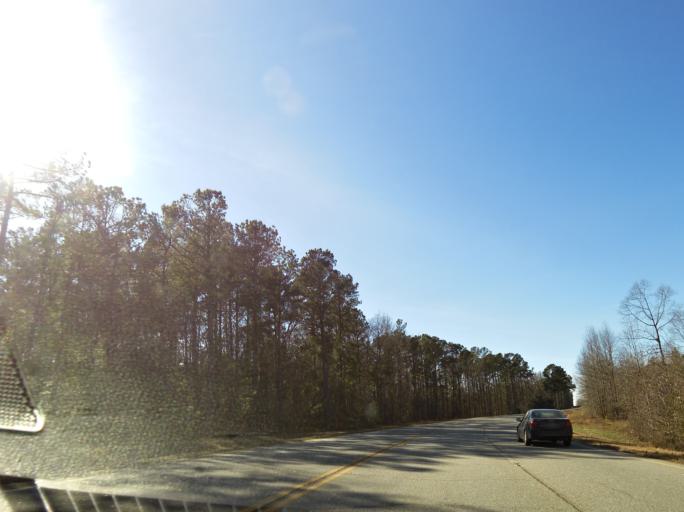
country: US
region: Georgia
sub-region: Crawford County
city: Roberta
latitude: 32.8724
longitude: -84.0418
